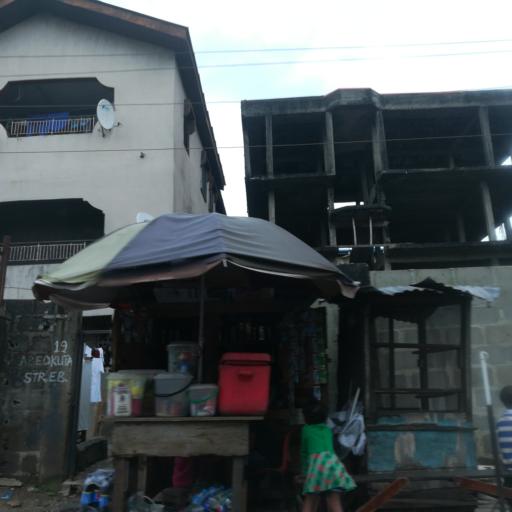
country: NG
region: Lagos
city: Ebute Metta
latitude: 6.4866
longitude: 3.3828
